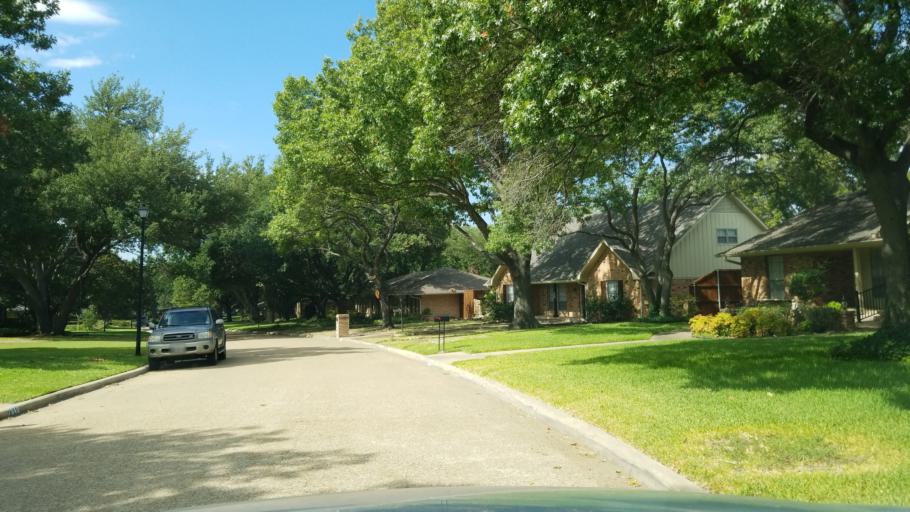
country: US
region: Texas
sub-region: Dallas County
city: Richardson
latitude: 32.9577
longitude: -96.7711
